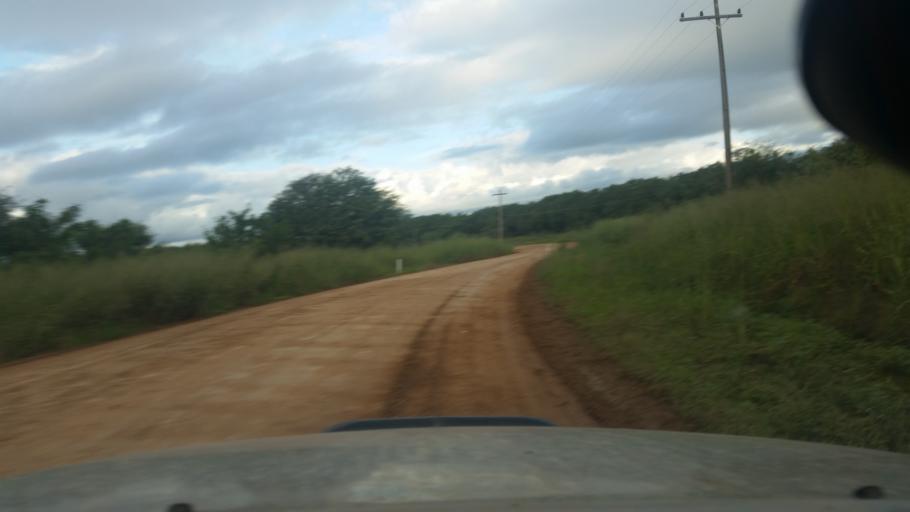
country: PY
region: Boqueron
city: Colonia Menno
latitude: -22.5858
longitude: -59.7300
